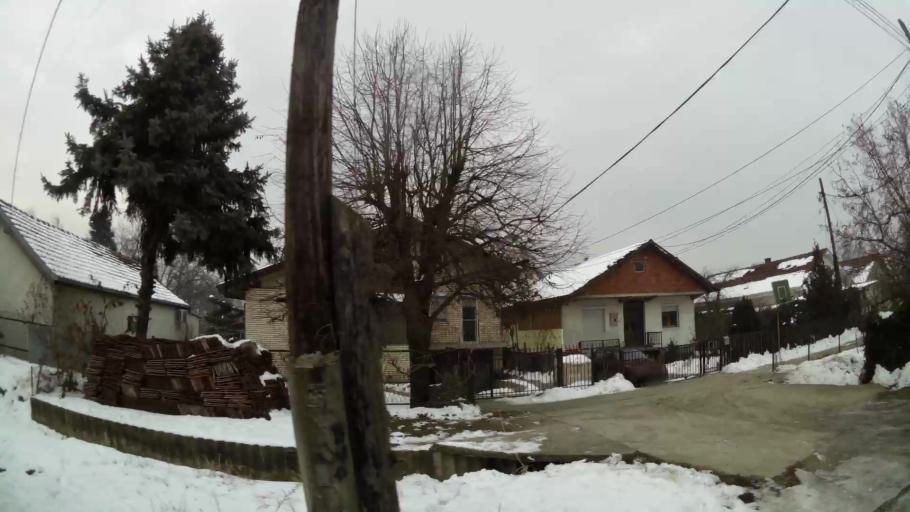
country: MK
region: Saraj
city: Saraj
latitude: 42.0318
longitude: 21.3542
